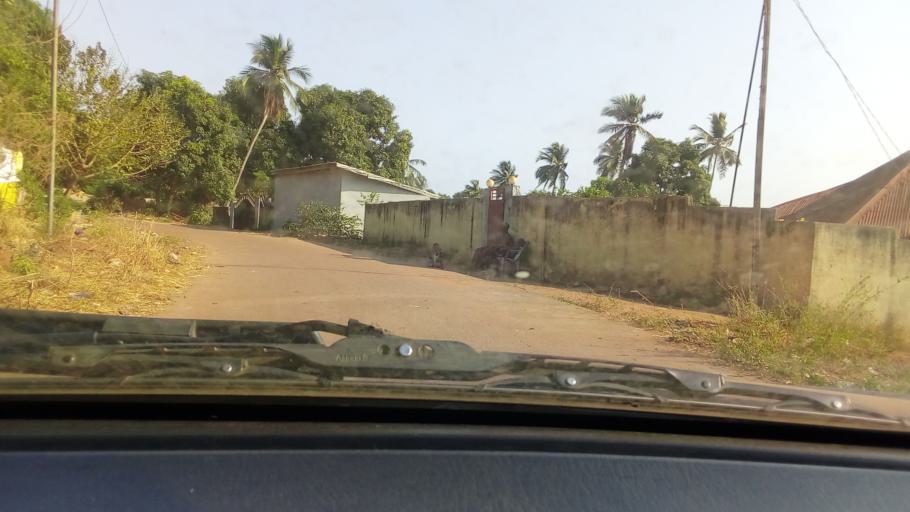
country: GN
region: Kindia
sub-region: Prefecture de Dubreka
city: Dubreka
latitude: 9.7883
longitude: -13.5274
